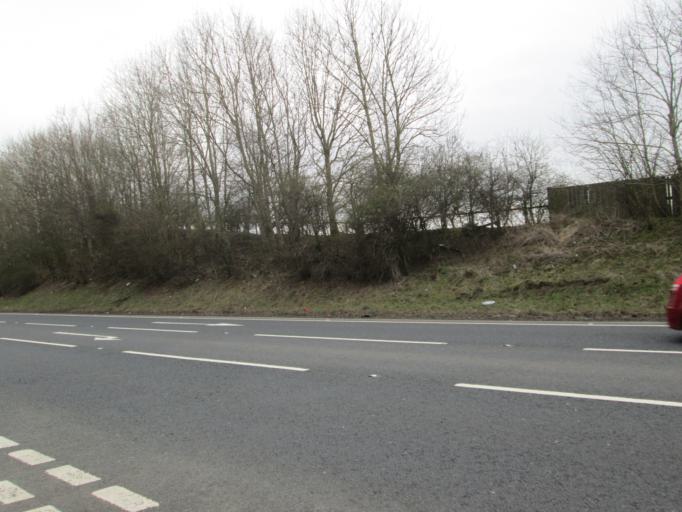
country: GB
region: England
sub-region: Northumberland
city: Bardon Mill
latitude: 54.9767
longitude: -2.3539
